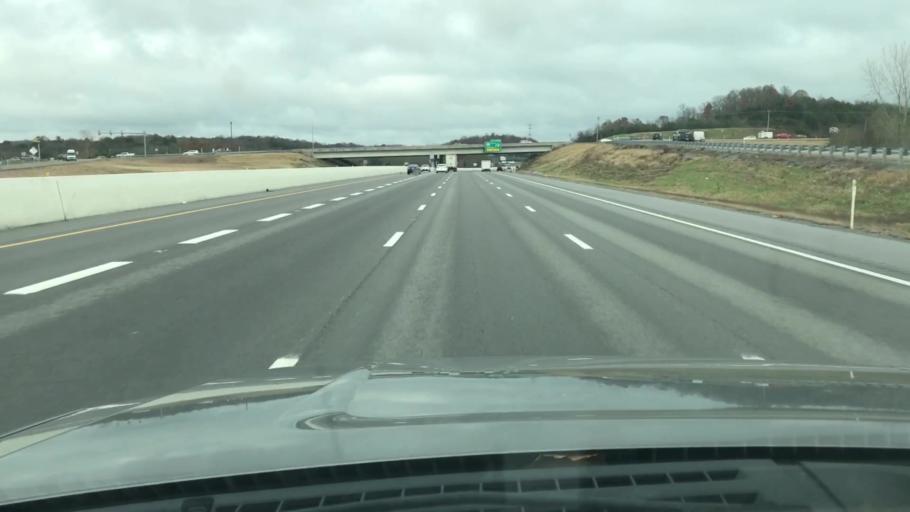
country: US
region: Tennessee
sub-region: Wilson County
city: Rural Hill
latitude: 36.1836
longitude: -86.4104
